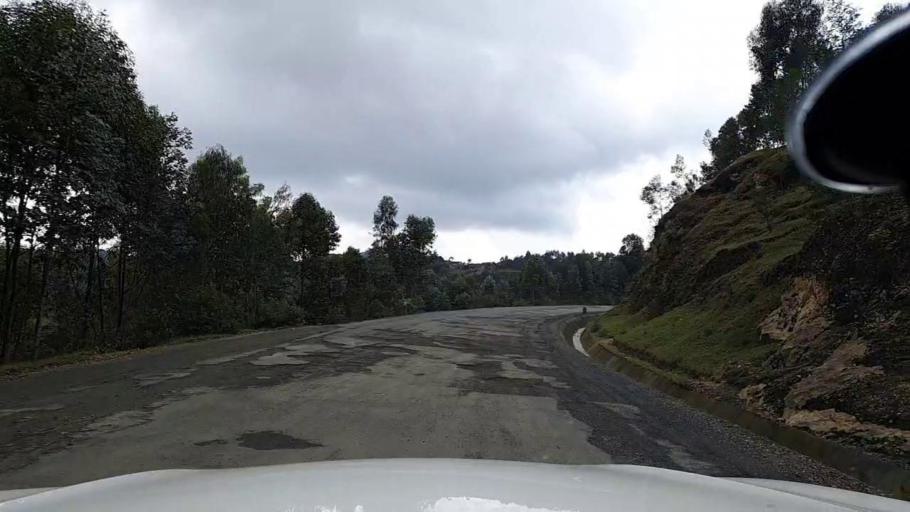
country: RW
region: Western Province
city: Kibuye
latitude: -2.0584
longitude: 29.5200
